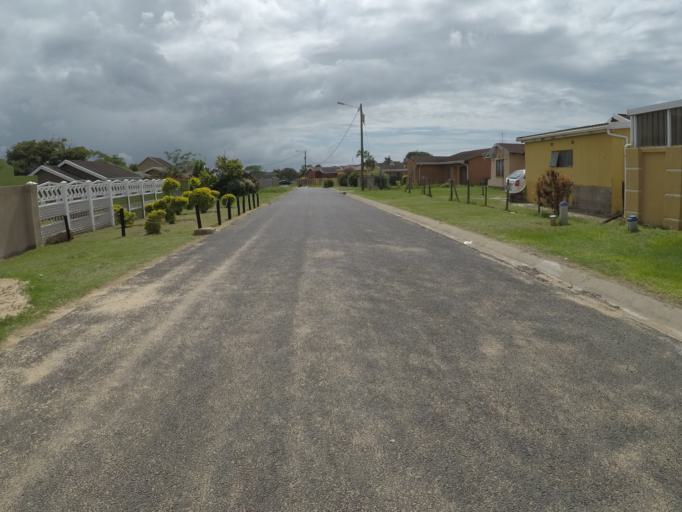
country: ZA
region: KwaZulu-Natal
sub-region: uThungulu District Municipality
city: eSikhawini
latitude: -28.8624
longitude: 31.9157
